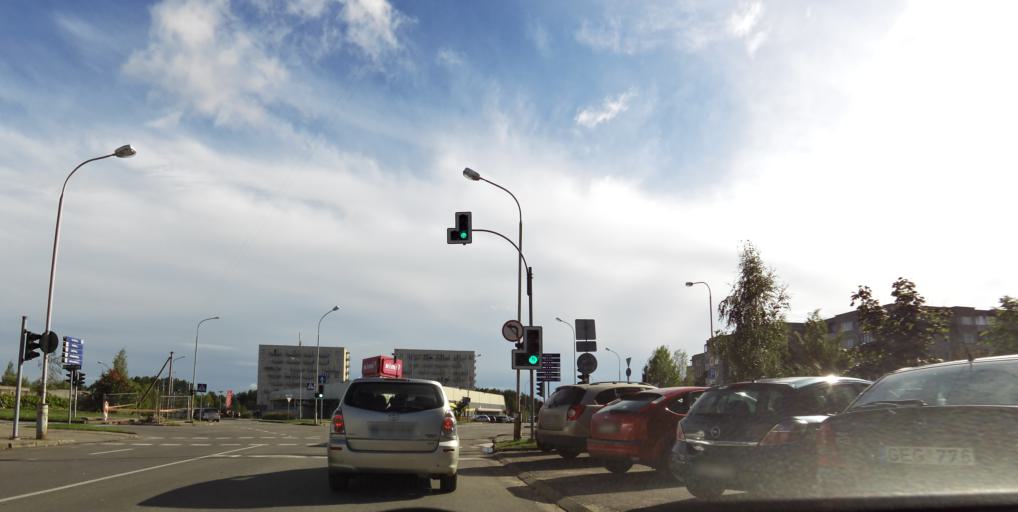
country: LT
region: Vilnius County
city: Pilaite
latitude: 54.7072
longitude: 25.1860
